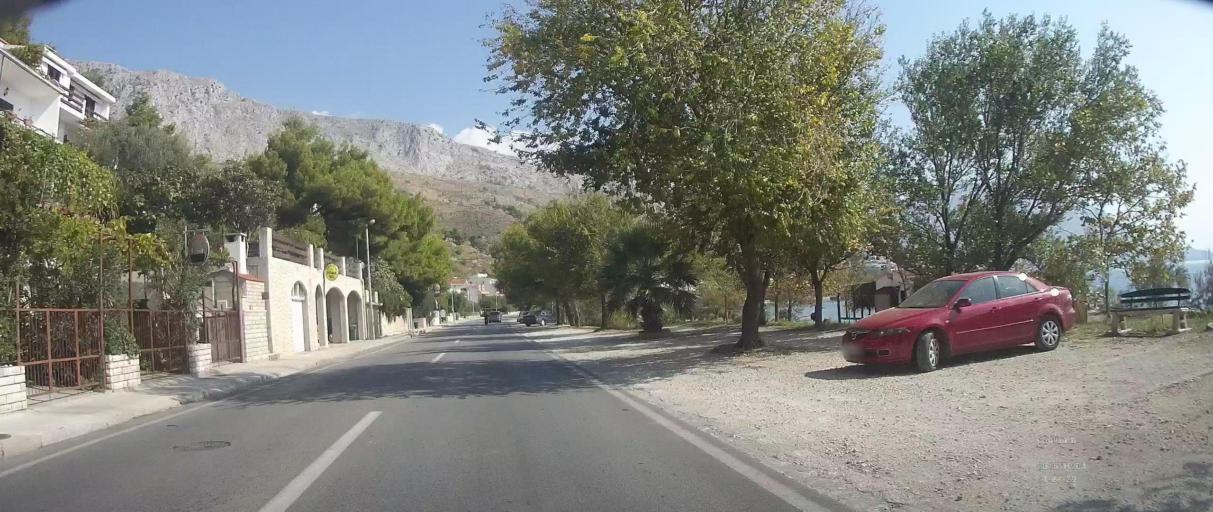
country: HR
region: Splitsko-Dalmatinska
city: Duce
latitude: 43.4406
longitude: 16.6488
